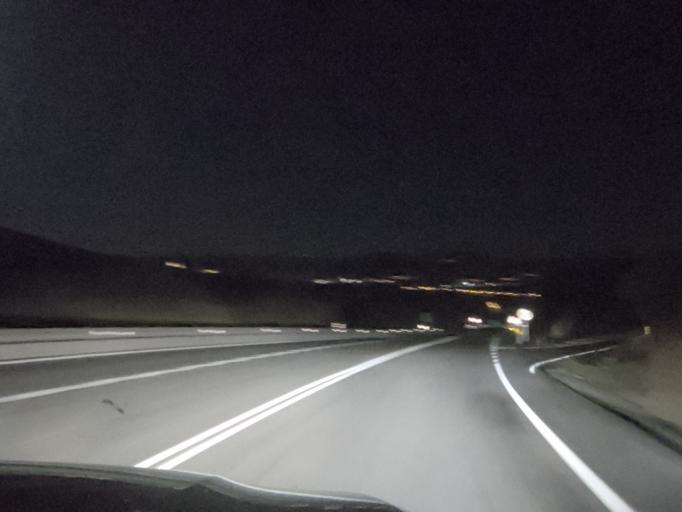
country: ES
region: Galicia
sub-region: Provincia de Ourense
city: Verin
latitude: 41.9613
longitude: -7.5059
